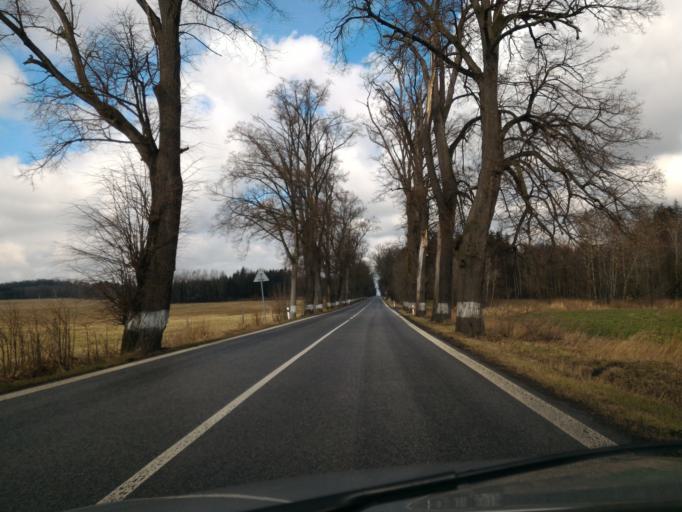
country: PL
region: Silesian Voivodeship
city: Zawidow
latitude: 50.9923
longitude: 15.0763
